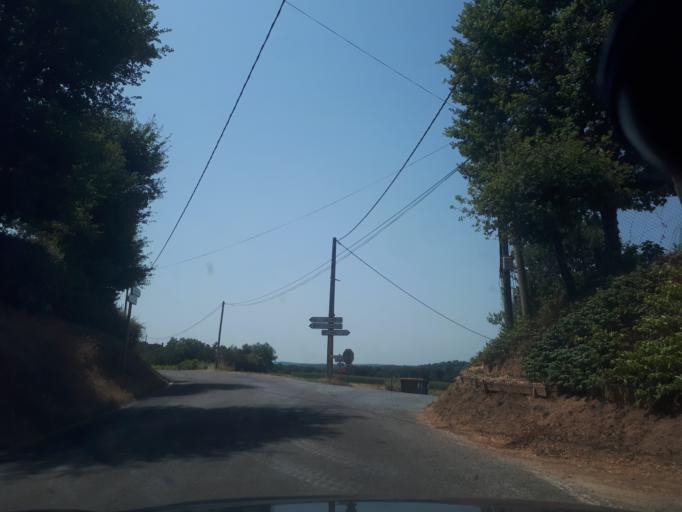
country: FR
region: Midi-Pyrenees
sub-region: Departement du Lot
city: Gourdon
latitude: 44.8230
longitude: 1.3785
